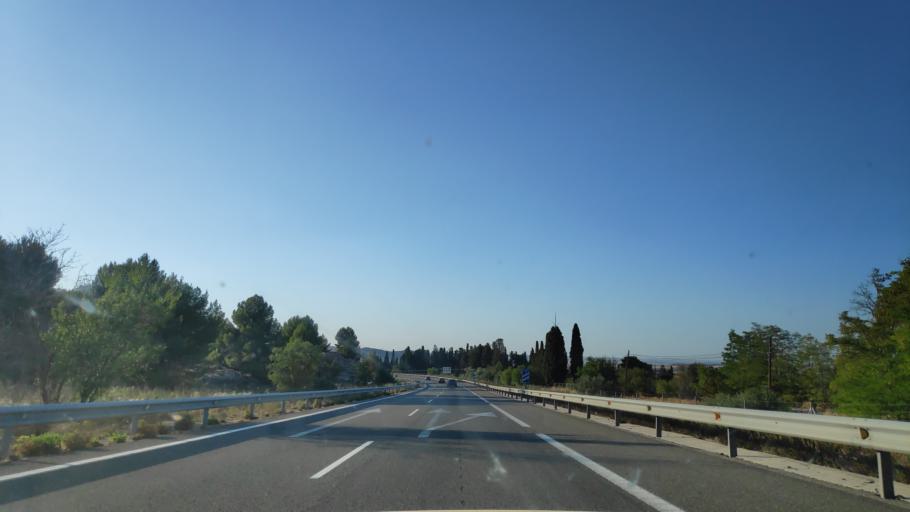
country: ES
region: Castille-La Mancha
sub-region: Provincia de Cuenca
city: Belinchon
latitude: 40.0260
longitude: -3.0358
